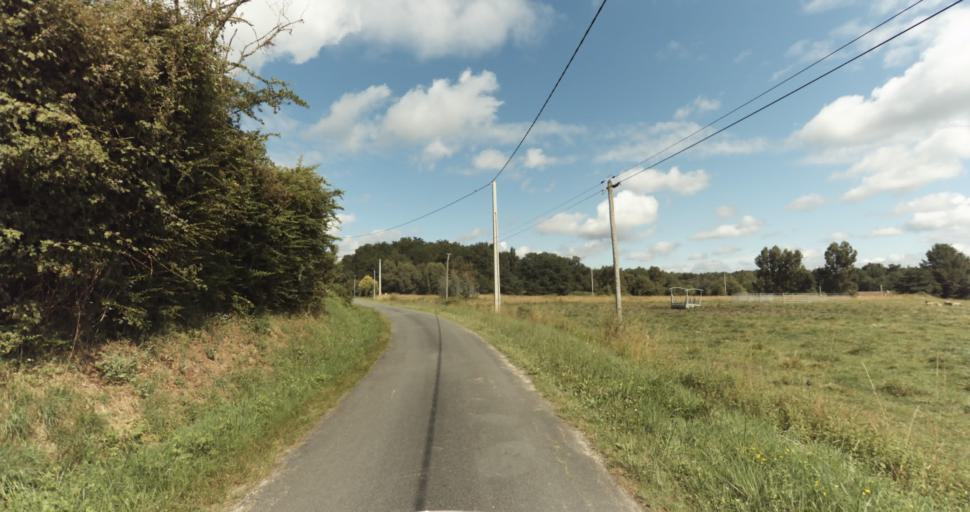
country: FR
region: Aquitaine
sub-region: Departement de la Gironde
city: Bazas
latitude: 44.4468
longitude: -0.1993
